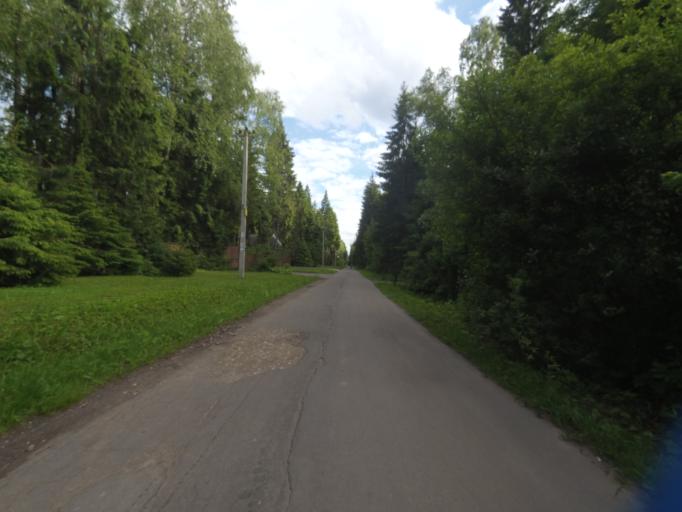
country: RU
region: Moskovskaya
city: Nekrasovskiy
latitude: 56.1154
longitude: 37.5172
